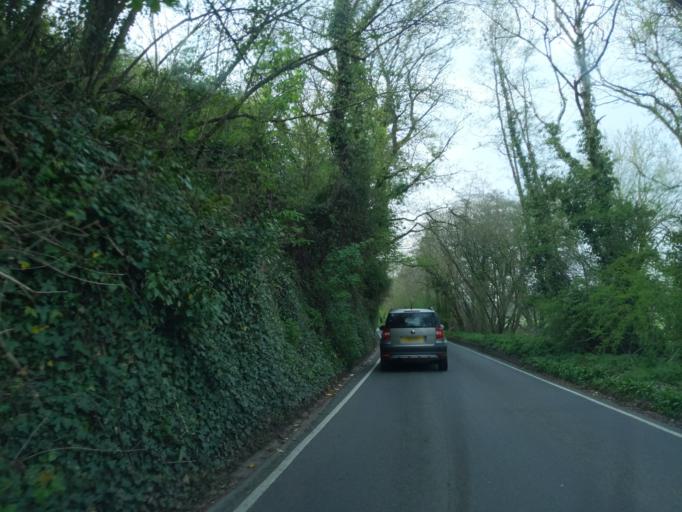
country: GB
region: England
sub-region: Devon
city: Exeter
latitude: 50.7381
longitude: -3.5503
